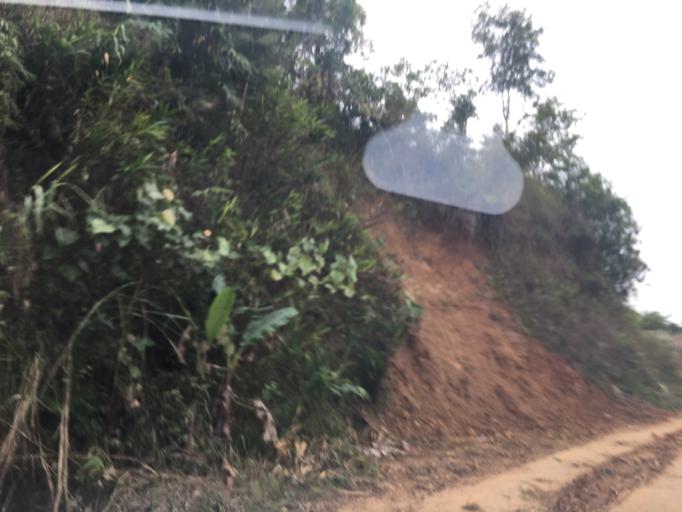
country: LA
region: Houaphan
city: Viengthong
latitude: 19.9354
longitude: 103.2993
